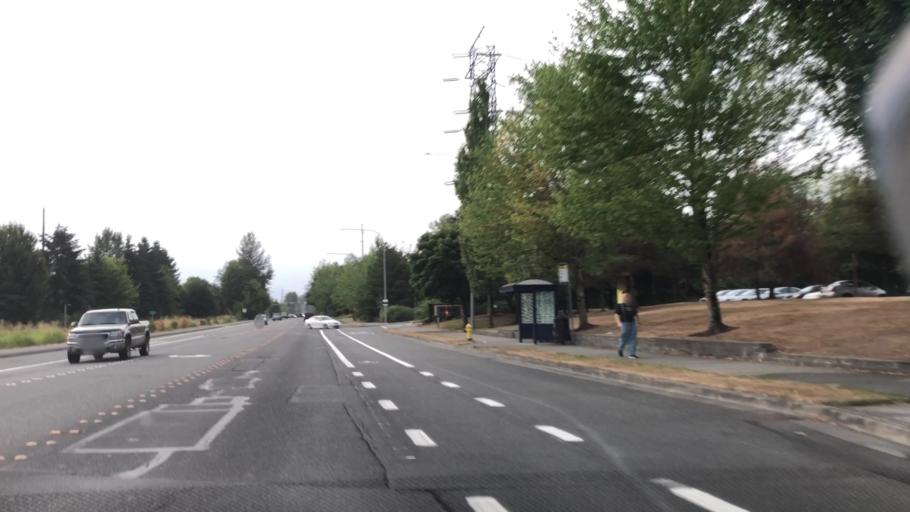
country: US
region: Washington
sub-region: King County
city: Redmond
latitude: 47.6882
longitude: -122.1485
